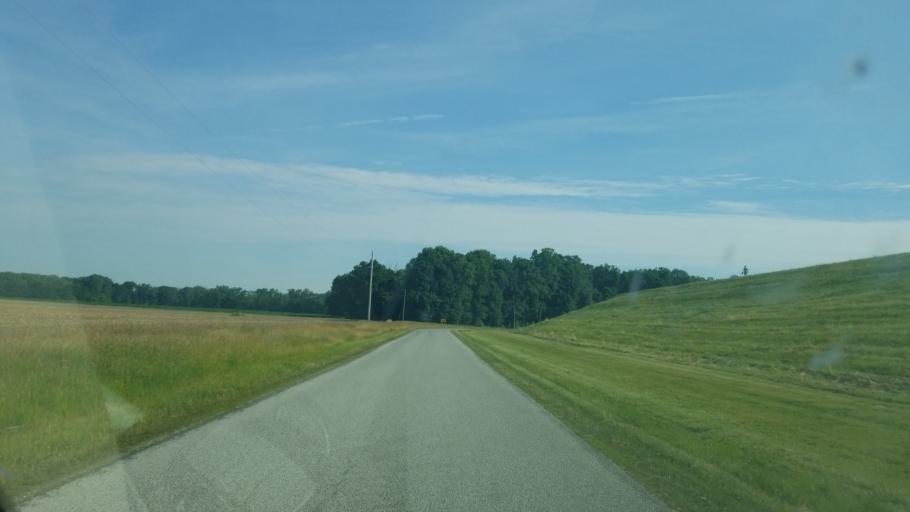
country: US
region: Ohio
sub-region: Hancock County
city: Findlay
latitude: 41.0265
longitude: -83.5807
